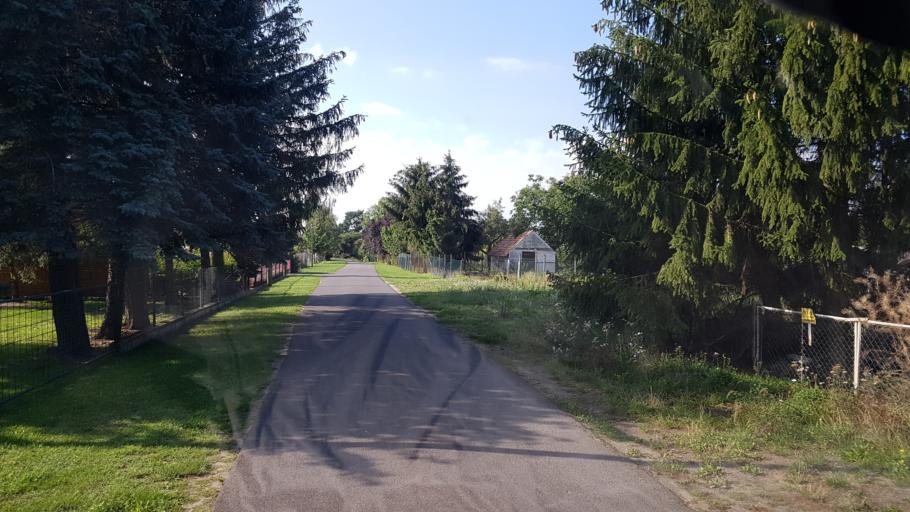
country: DE
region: Brandenburg
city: Luebben
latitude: 51.8816
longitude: 13.8457
